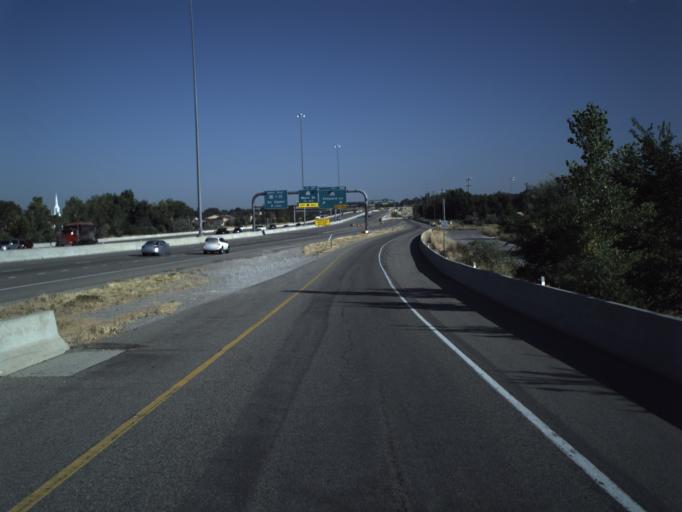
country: US
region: Utah
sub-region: Davis County
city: Farmington
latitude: 40.9935
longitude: -111.9035
